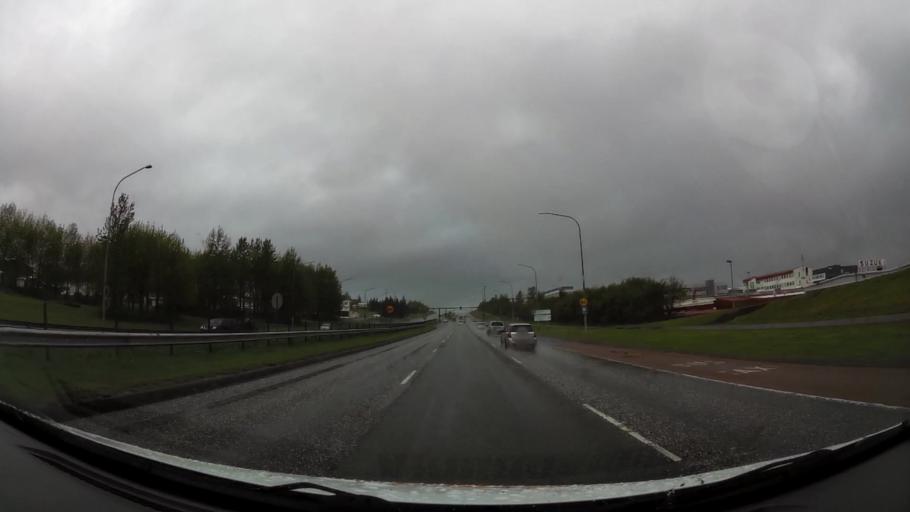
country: IS
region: Capital Region
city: Reykjavik
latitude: 64.1289
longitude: -21.8715
